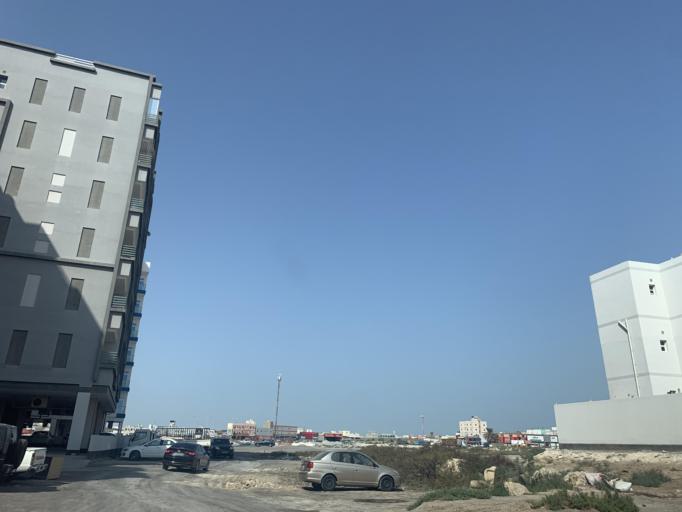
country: BH
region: Central Governorate
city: Madinat Hamad
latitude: 26.1364
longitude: 50.4894
